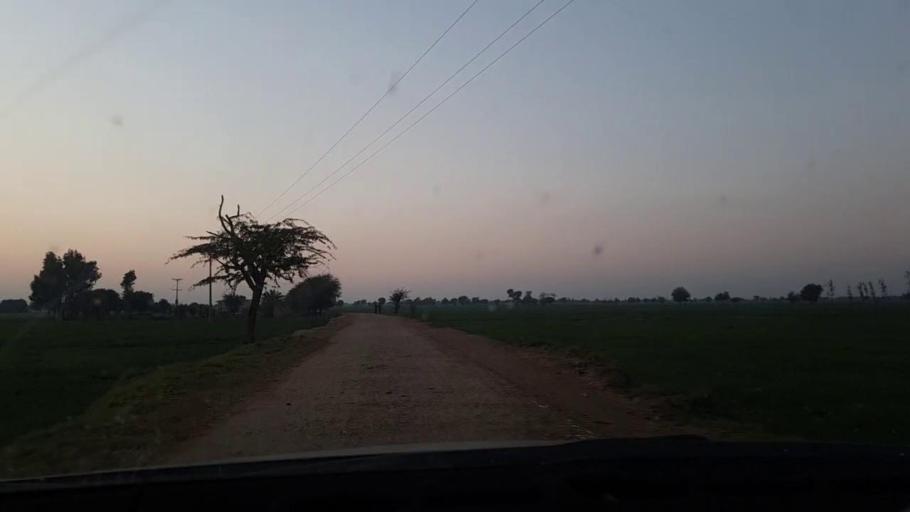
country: PK
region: Sindh
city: Tando Mittha Khan
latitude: 25.9295
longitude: 69.3300
